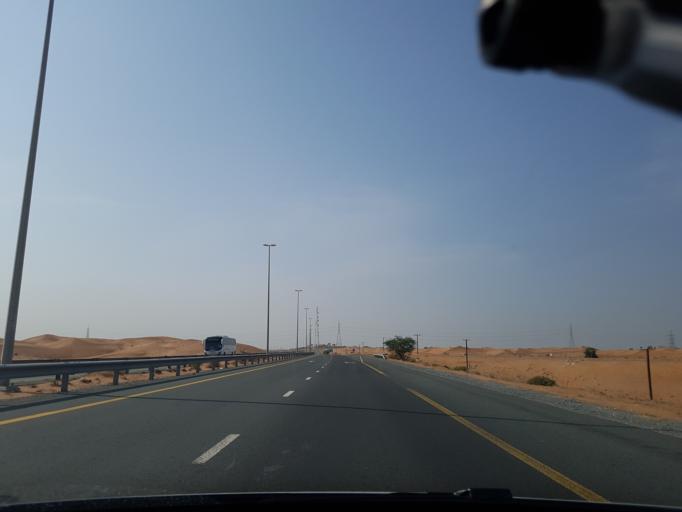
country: AE
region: Umm al Qaywayn
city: Umm al Qaywayn
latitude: 25.5234
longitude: 55.7353
